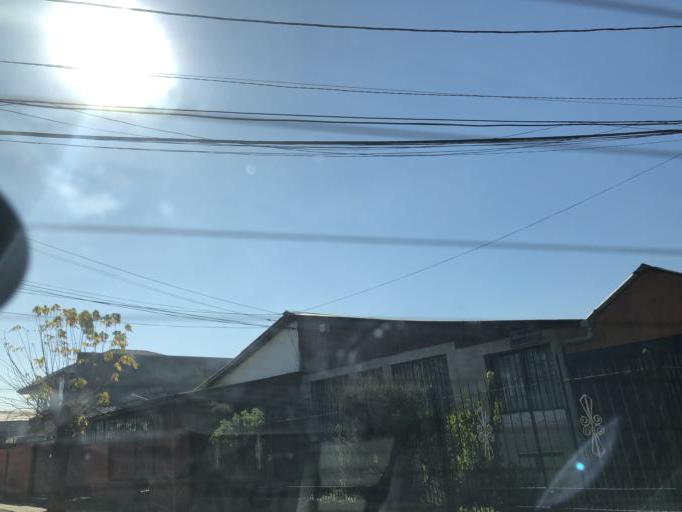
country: CL
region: Santiago Metropolitan
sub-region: Provincia de Cordillera
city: Puente Alto
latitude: -33.6083
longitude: -70.5934
